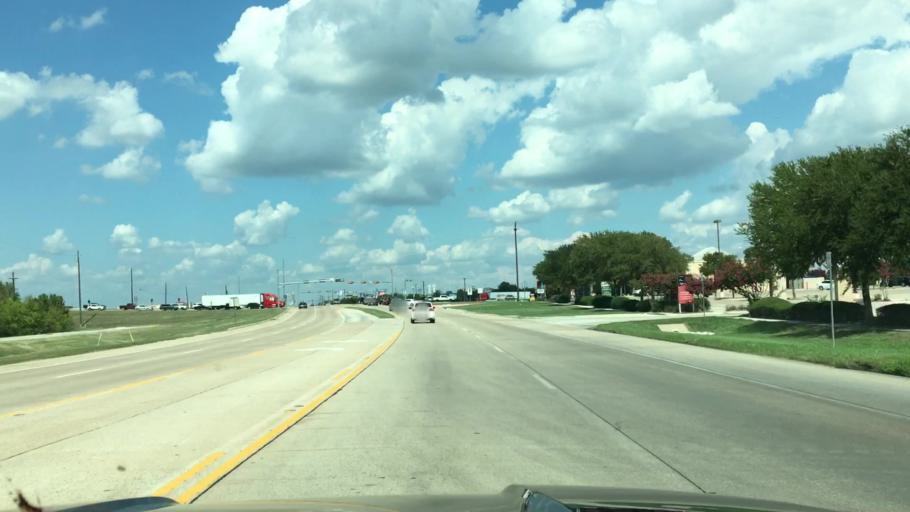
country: US
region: Texas
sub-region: Denton County
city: Roanoke
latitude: 33.0098
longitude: -97.2233
